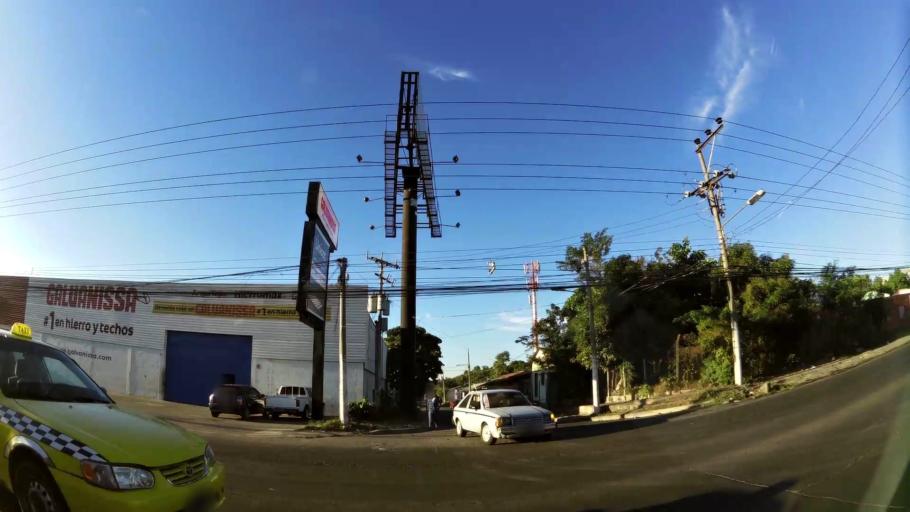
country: SV
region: San Miguel
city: San Miguel
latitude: 13.4662
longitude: -88.1735
